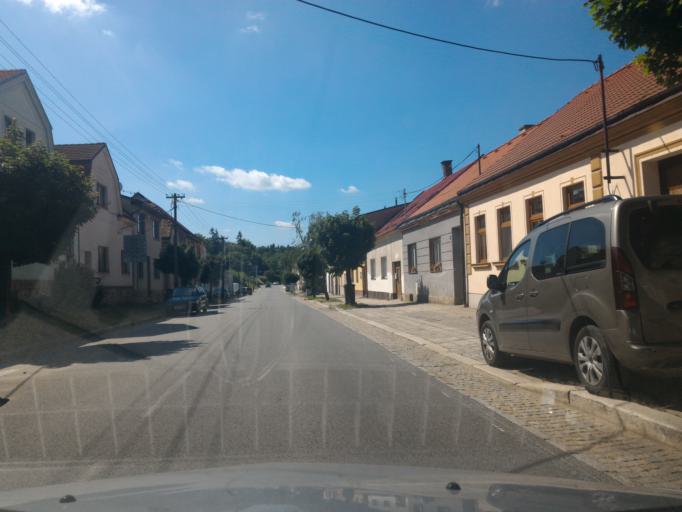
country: CZ
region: Vysocina
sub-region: Okres Jihlava
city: Telc
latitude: 49.1818
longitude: 15.4631
